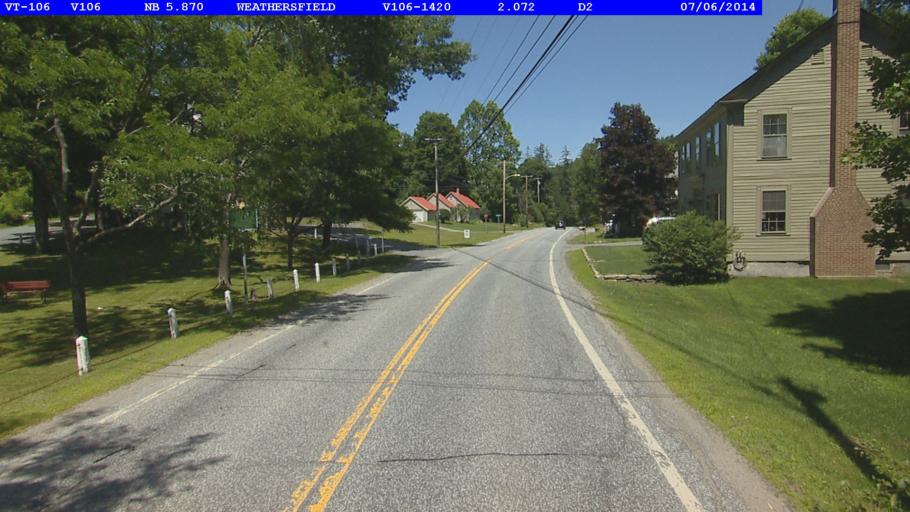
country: US
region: Vermont
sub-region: Windsor County
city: Springfield
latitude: 43.3719
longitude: -72.5160
